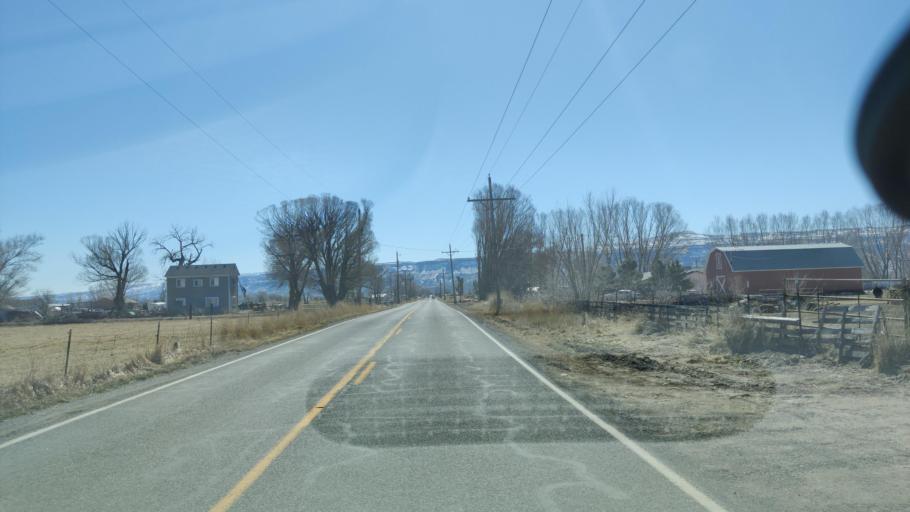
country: US
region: Colorado
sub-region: Mesa County
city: Fruita
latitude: 39.1629
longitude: -108.7012
